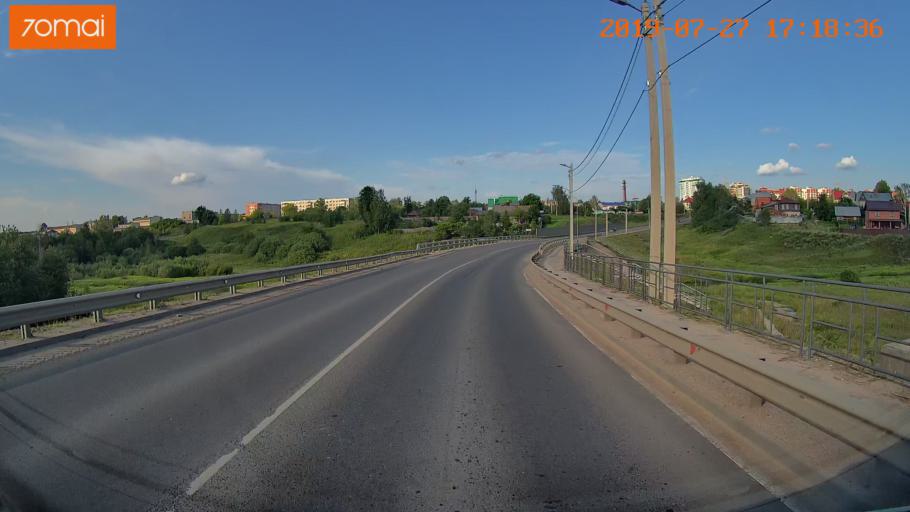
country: RU
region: Ivanovo
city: Novo-Talitsy
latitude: 57.0330
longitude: 40.9069
